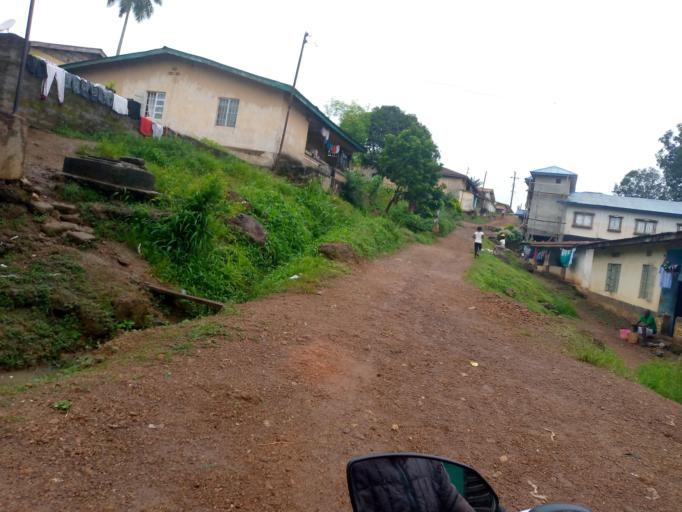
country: SL
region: Eastern Province
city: Kenema
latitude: 7.8781
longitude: -11.1833
